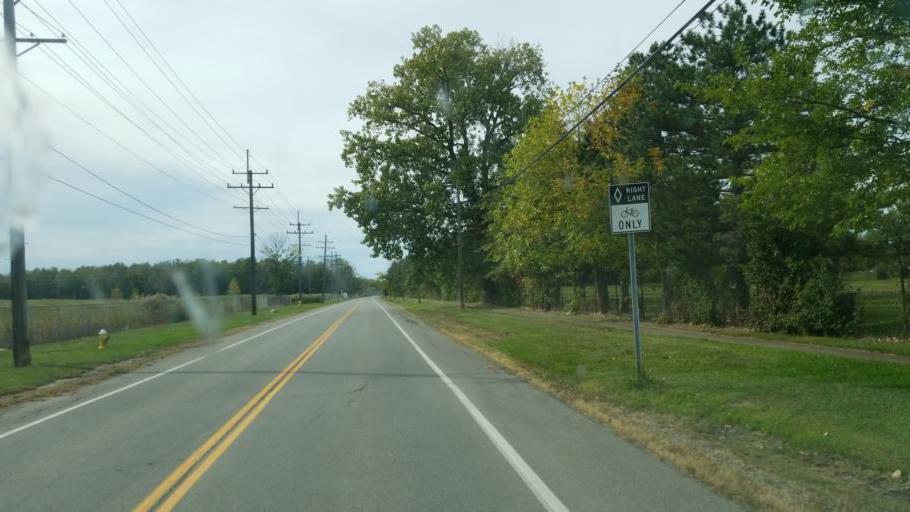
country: US
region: Ohio
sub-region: Lorain County
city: Avon Lake
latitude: 41.4935
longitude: -82.0633
